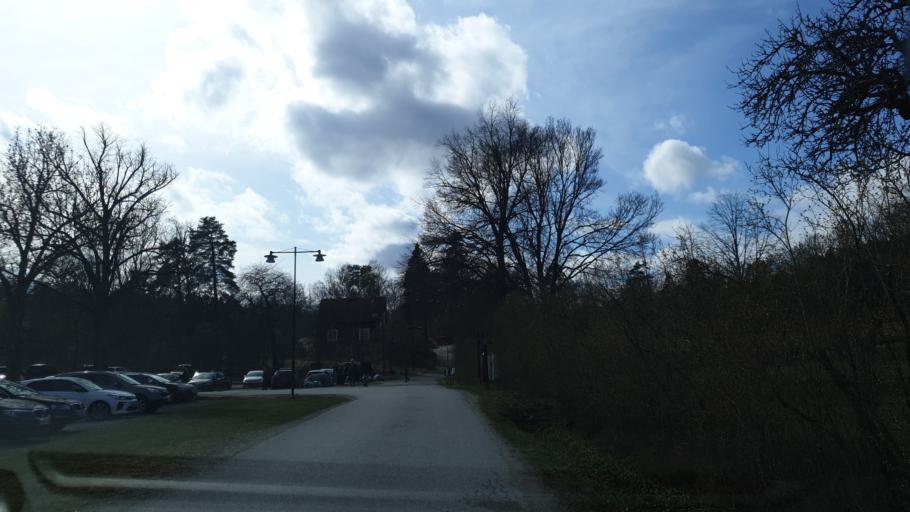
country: SE
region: Stockholm
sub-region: Nacka Kommun
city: Kummelnas
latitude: 59.3461
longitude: 18.3235
